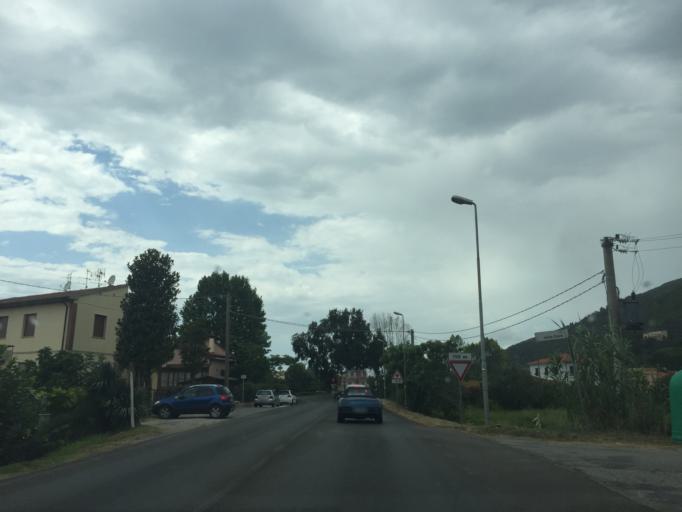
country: IT
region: Tuscany
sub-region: Province of Pisa
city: San Giuliano Terme
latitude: 43.7586
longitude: 10.4429
